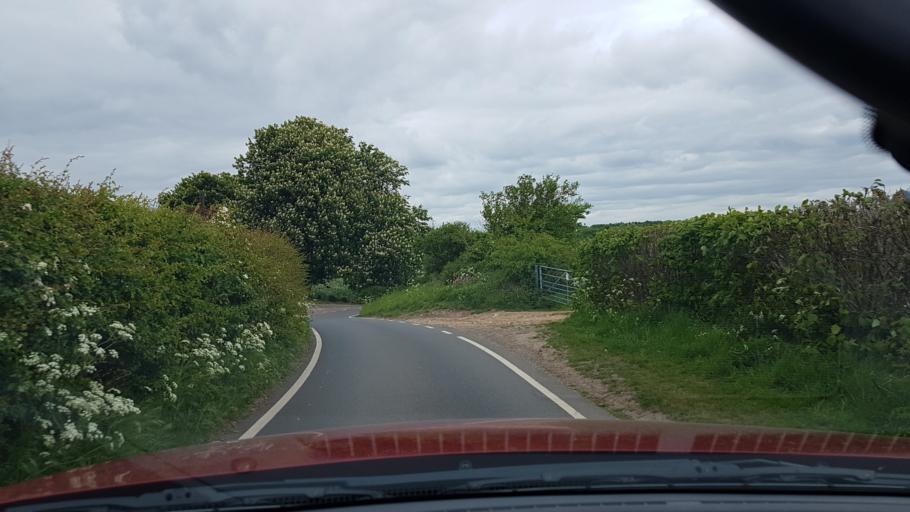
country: GB
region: England
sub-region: Rotherham
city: Maltby
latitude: 53.4042
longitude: -1.1948
